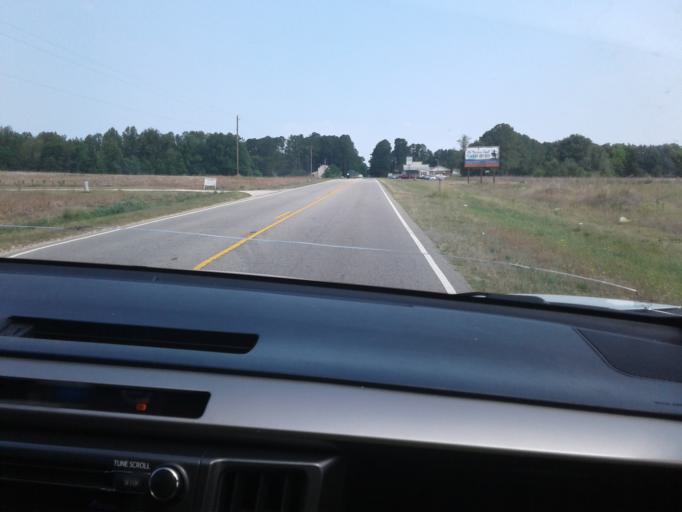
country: US
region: North Carolina
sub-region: Harnett County
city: Coats
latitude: 35.4226
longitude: -78.6760
